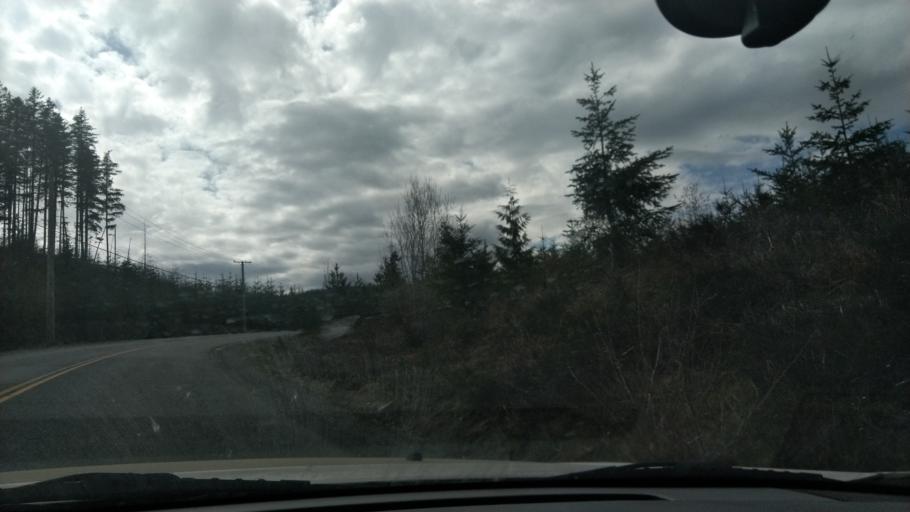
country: CA
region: British Columbia
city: Campbell River
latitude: 49.9997
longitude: -125.3749
